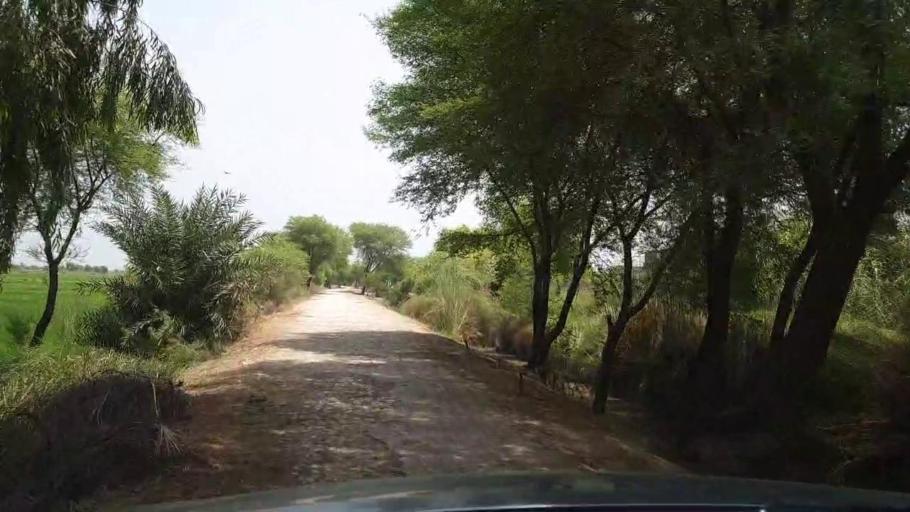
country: PK
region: Sindh
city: Madeji
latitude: 27.7776
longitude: 68.4012
